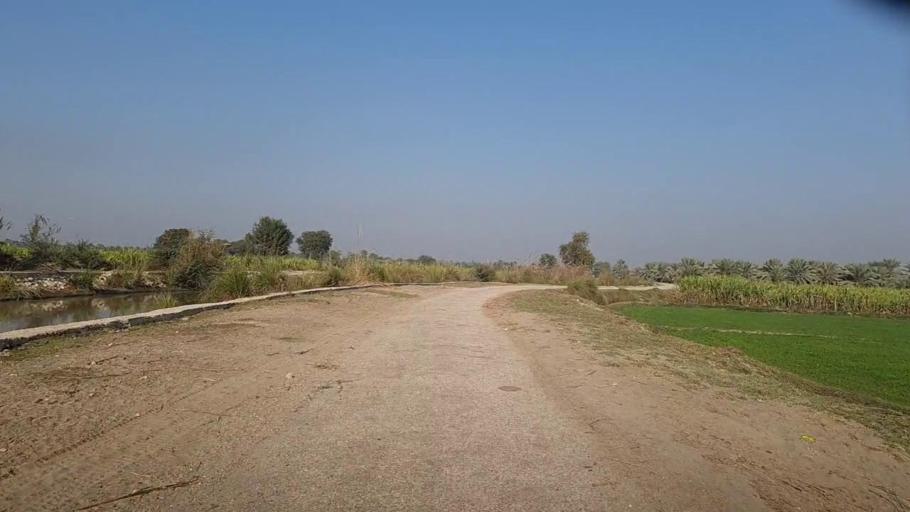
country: PK
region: Sindh
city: Ranipur
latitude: 27.2478
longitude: 68.5554
